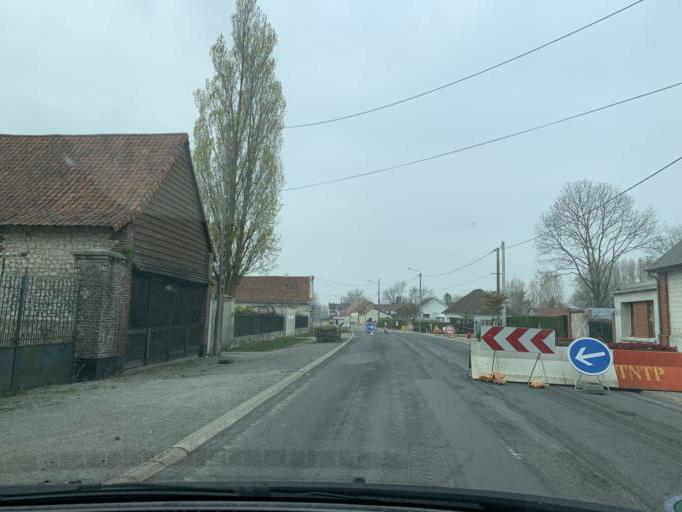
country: FR
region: Nord-Pas-de-Calais
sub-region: Departement du Pas-de-Calais
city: Montreuil
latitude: 50.4078
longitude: 1.7251
